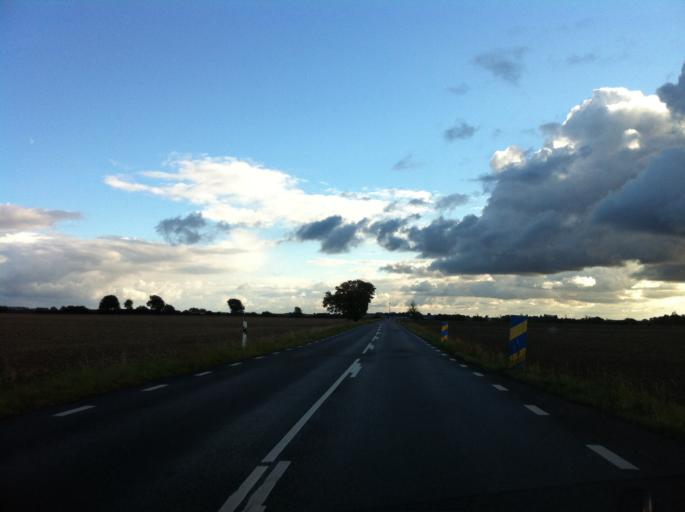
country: SE
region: Skane
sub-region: Svalovs Kommun
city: Svaloev
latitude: 55.9220
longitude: 13.2037
